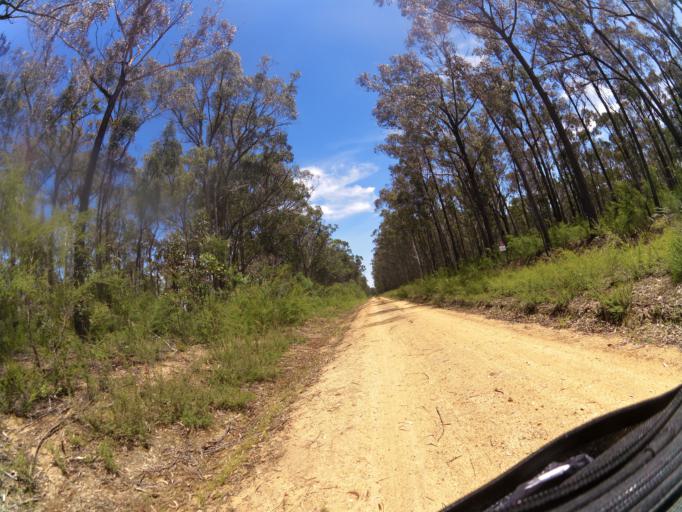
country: AU
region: Victoria
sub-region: East Gippsland
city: Lakes Entrance
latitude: -37.7569
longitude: 147.9638
